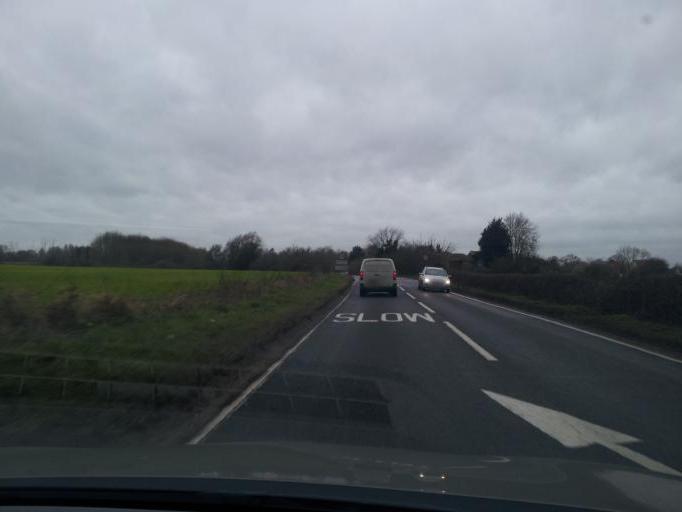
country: GB
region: England
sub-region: Norfolk
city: Diss
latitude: 52.3540
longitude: 1.0681
